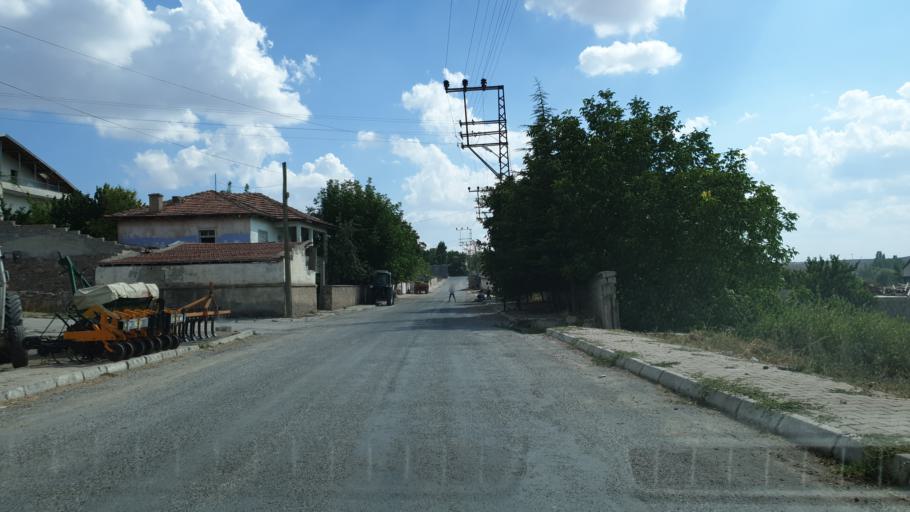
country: TR
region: Kayseri
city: Felahiye
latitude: 39.0923
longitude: 35.5630
